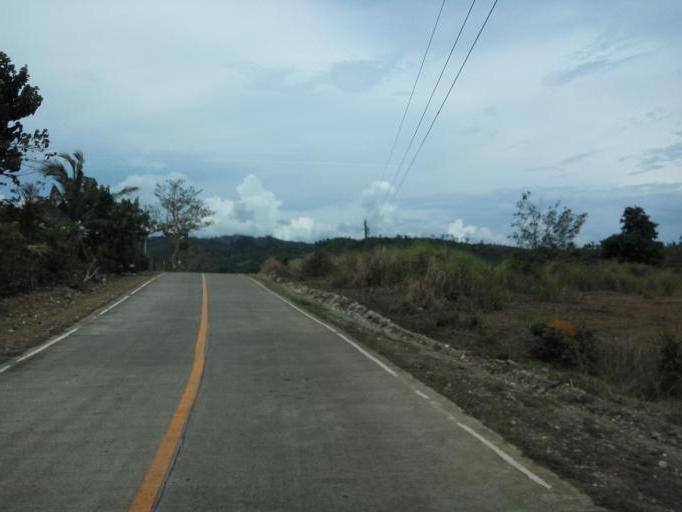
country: PH
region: Cagayan Valley
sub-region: Province of Quirino
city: Dumabato
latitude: 16.2573
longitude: 121.6691
